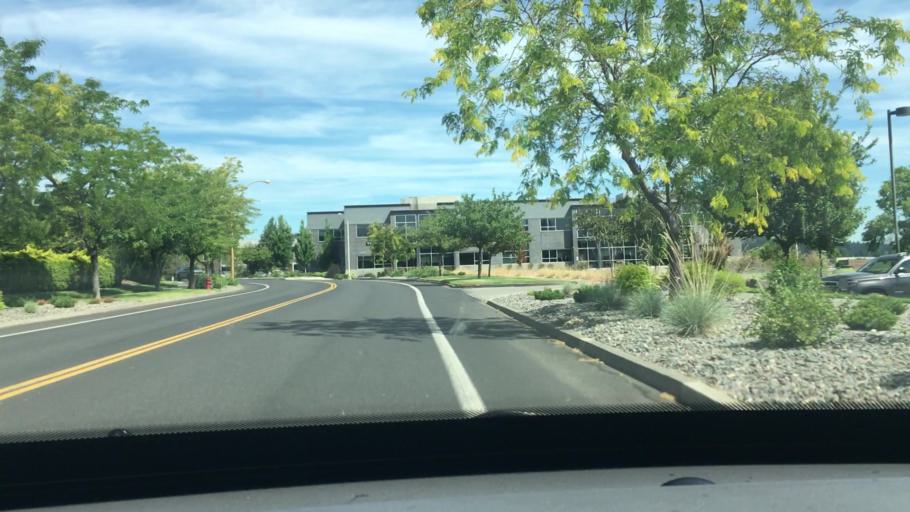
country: US
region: Oregon
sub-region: Deschutes County
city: Bend
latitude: 44.0442
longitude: -121.3254
